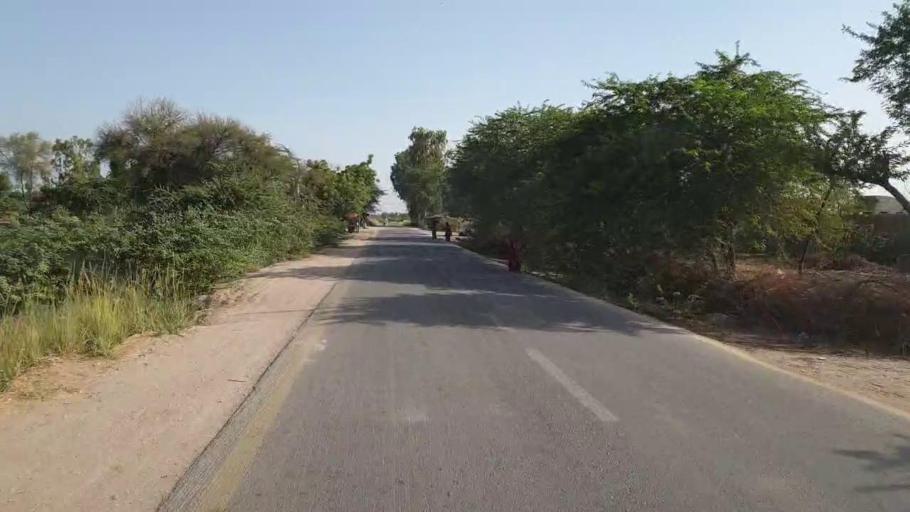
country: PK
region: Sindh
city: Daur
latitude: 26.4625
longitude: 68.4514
